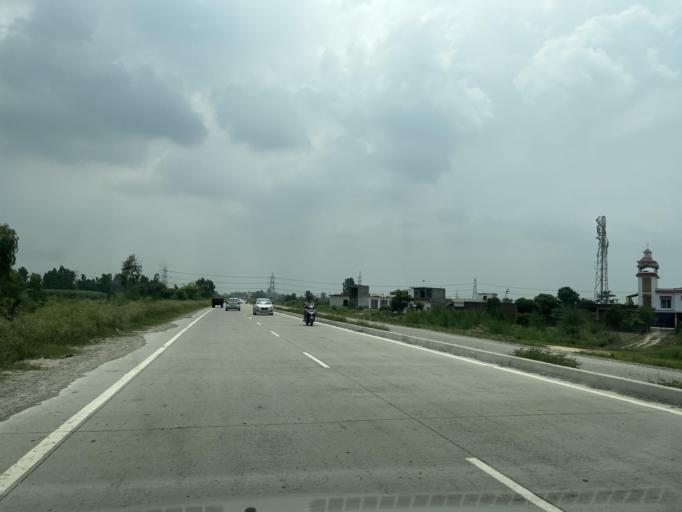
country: IN
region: Uttar Pradesh
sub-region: Bijnor
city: Najibabad
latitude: 29.5709
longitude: 78.3389
